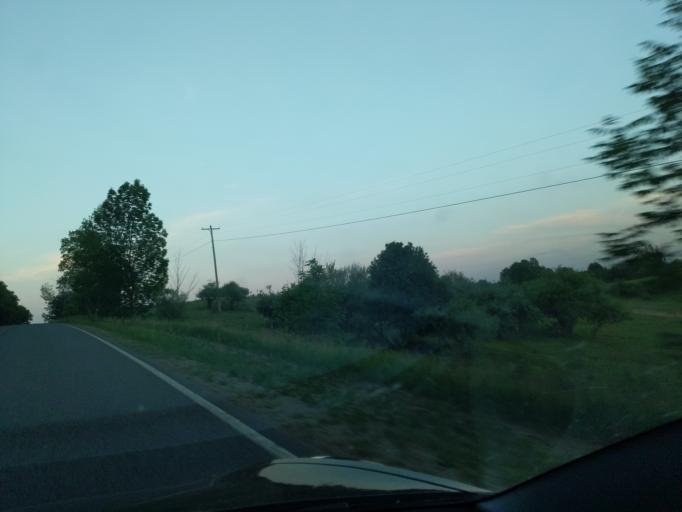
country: US
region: Michigan
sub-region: Barry County
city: Nashville
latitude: 42.5378
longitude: -85.0923
